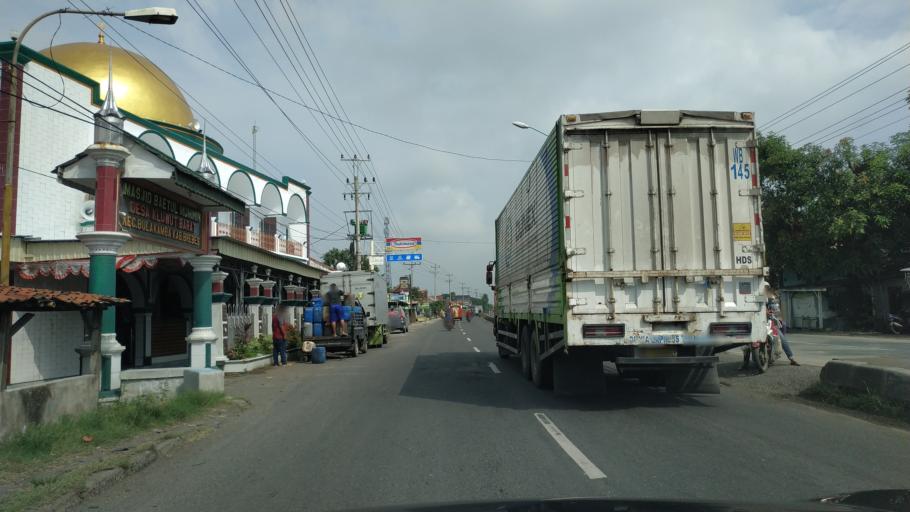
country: ID
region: Central Java
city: Bulakamba
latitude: -6.8744
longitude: 108.9164
